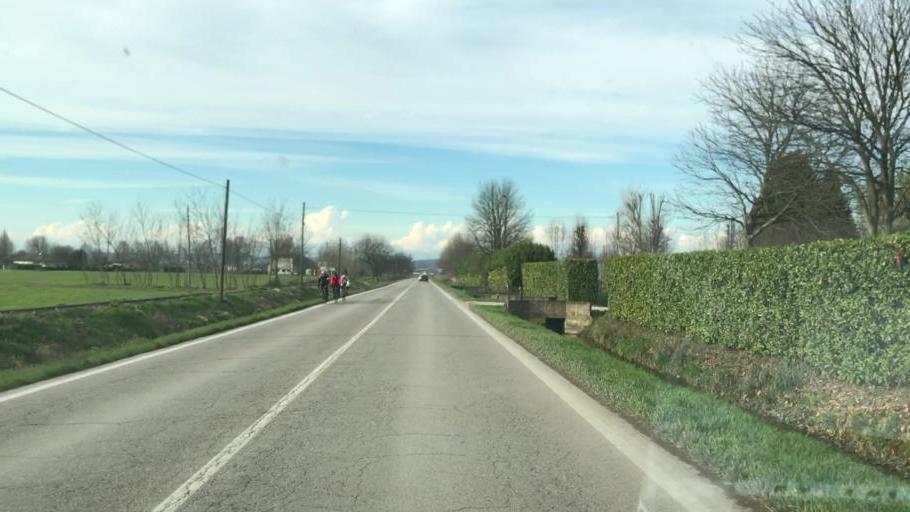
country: IT
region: Lombardy
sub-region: Provincia di Mantova
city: Cerlongo
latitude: 45.2875
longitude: 10.6570
